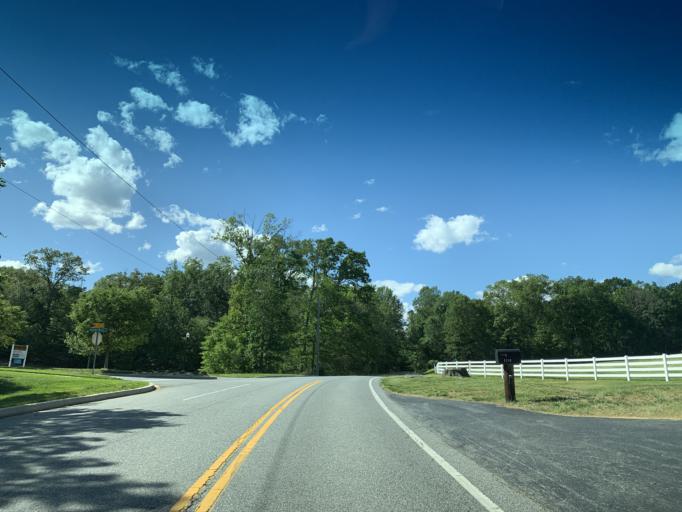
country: US
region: Maryland
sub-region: Cecil County
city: North East
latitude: 39.5496
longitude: -75.9213
